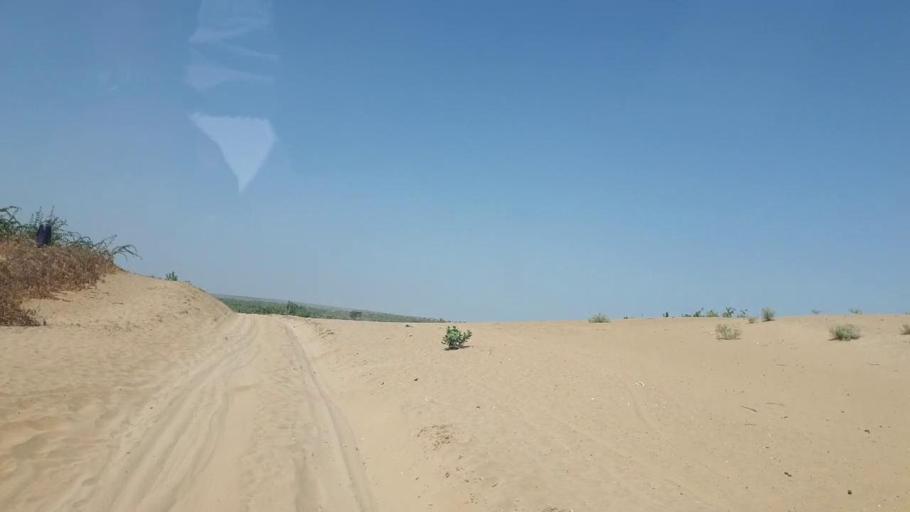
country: PK
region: Sindh
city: Chor
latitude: 25.3532
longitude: 70.3413
